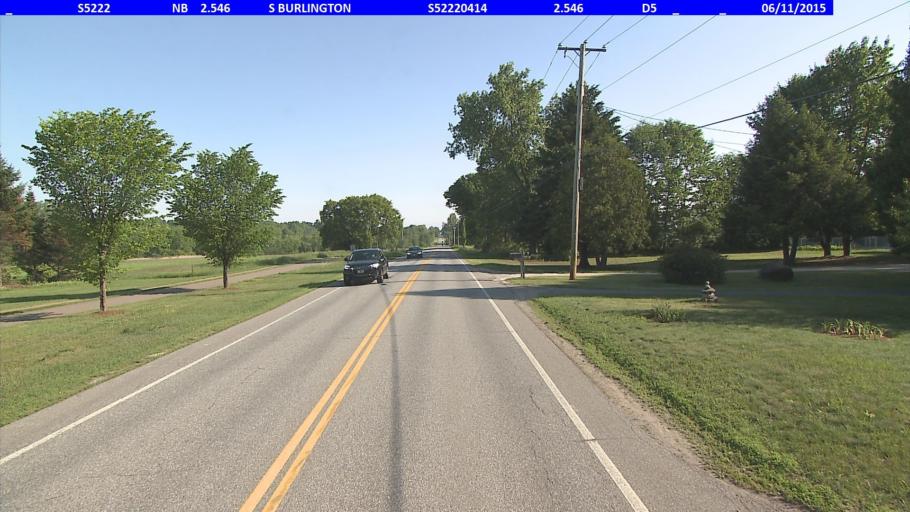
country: US
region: Vermont
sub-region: Chittenden County
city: South Burlington
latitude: 44.4532
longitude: -73.1889
